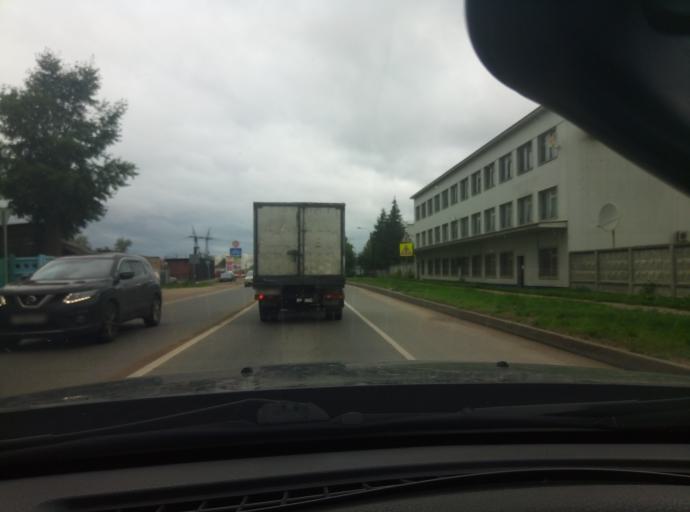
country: RU
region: Moskovskaya
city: Serpukhov
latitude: 54.9128
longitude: 37.4651
